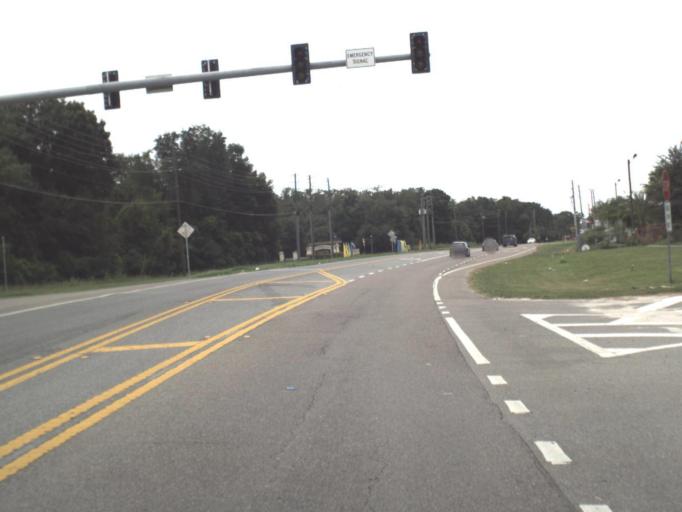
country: US
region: Florida
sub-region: Pasco County
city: Zephyrhills West
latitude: 28.2297
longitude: -82.2251
